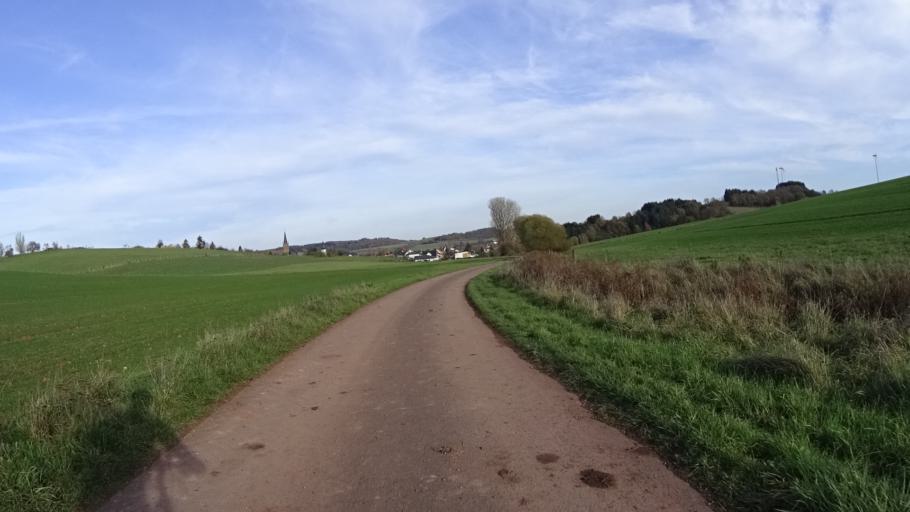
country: DE
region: Rheinland-Pfalz
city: Sien
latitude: 49.6880
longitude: 7.4938
